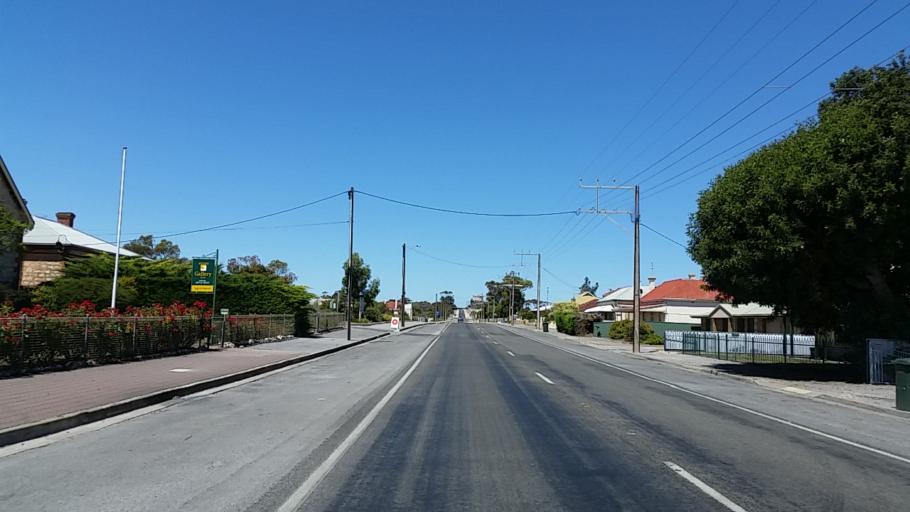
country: AU
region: South Australia
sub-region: Yorke Peninsula
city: Honiton
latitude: -35.0186
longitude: 137.6082
